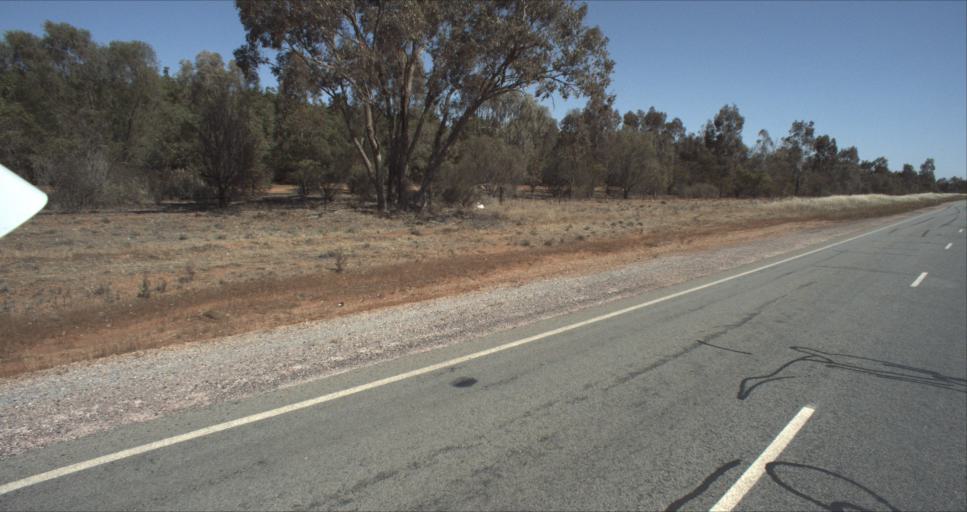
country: AU
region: New South Wales
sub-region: Leeton
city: Leeton
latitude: -34.5025
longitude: 146.4452
